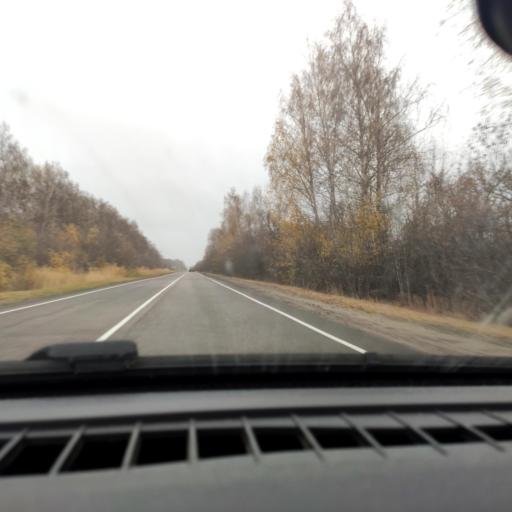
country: RU
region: Voronezj
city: Kolodeznyy
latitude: 51.3471
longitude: 39.0238
